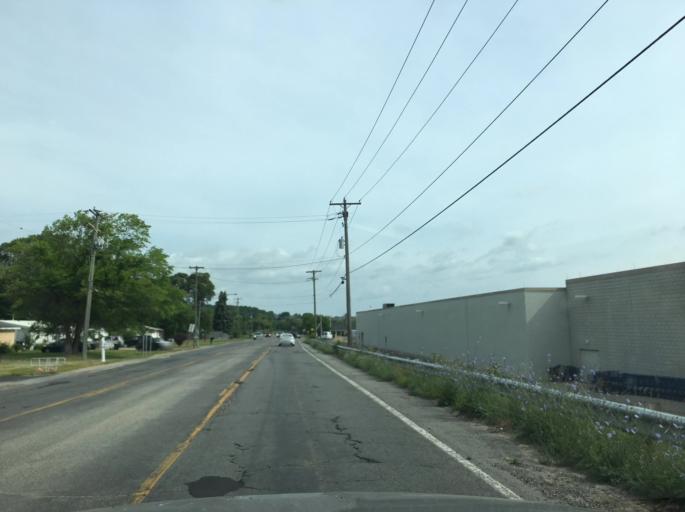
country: US
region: Michigan
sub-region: Grand Traverse County
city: Traverse City
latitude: 44.7430
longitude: -85.6455
